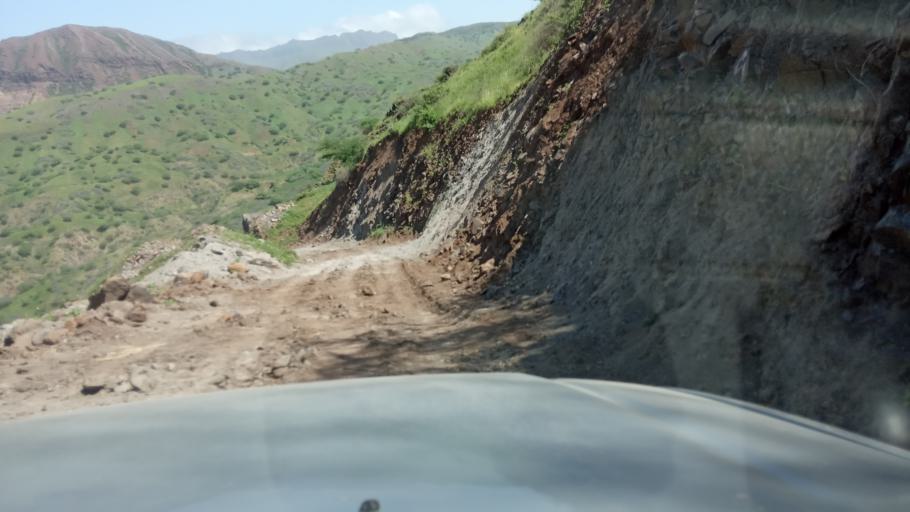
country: CV
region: Santa Catarina
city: Assomada
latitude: 15.1096
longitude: -23.7295
